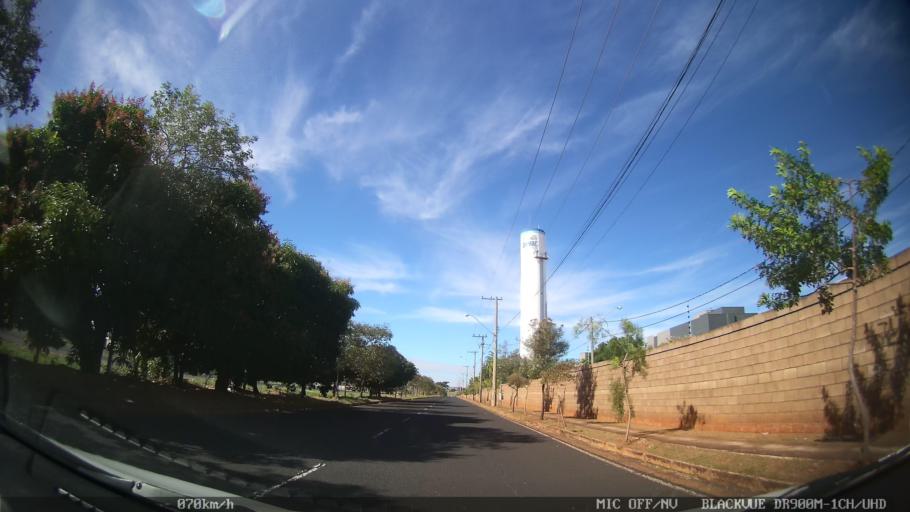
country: BR
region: Sao Paulo
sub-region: Sao Jose Do Rio Preto
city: Sao Jose do Rio Preto
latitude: -20.8008
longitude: -49.3392
